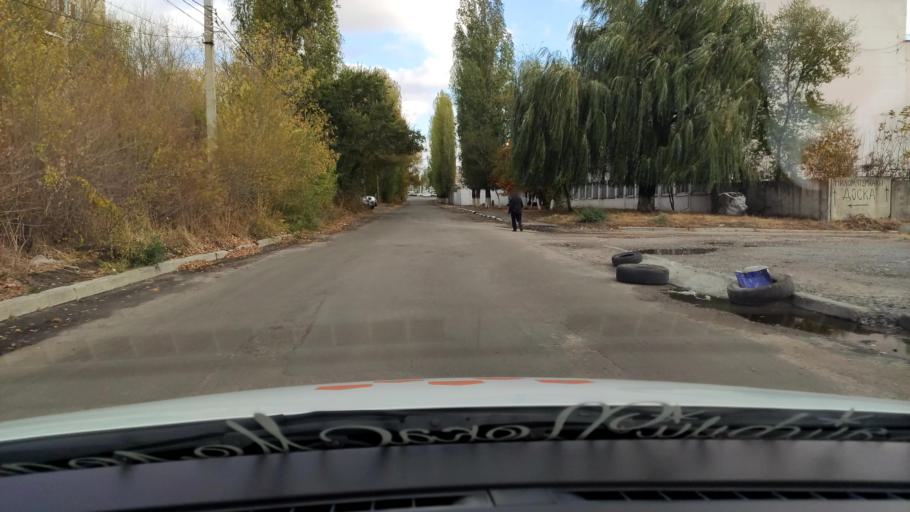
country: RU
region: Voronezj
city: Voronezh
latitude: 51.6433
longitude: 39.1326
